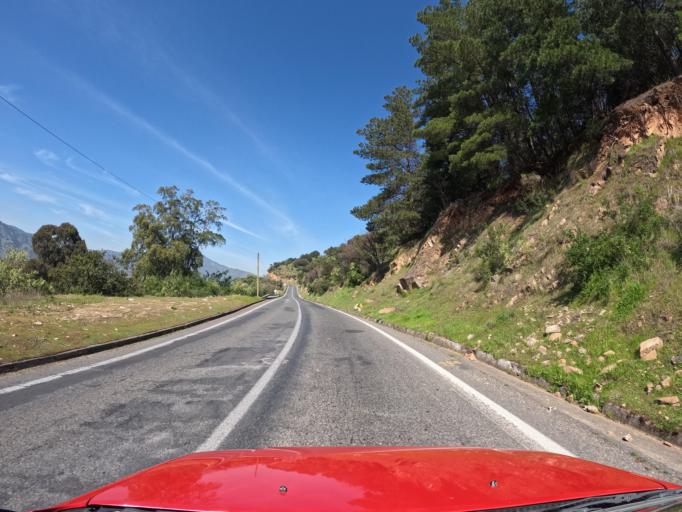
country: CL
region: Maule
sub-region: Provincia de Curico
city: Rauco
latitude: -35.0457
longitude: -71.5936
